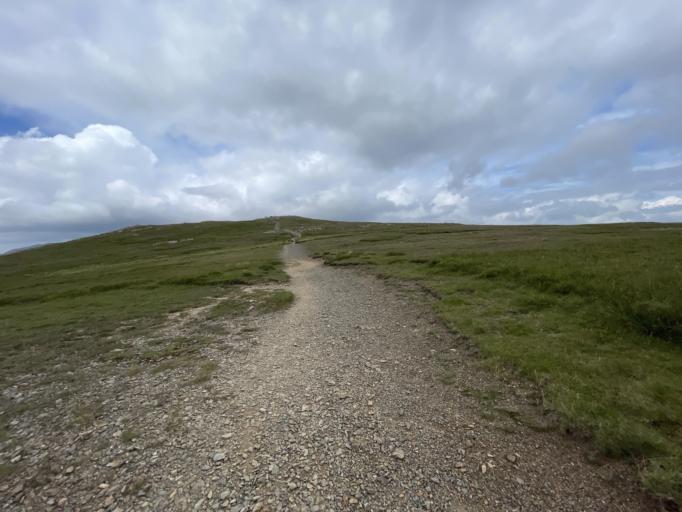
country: GB
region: England
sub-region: Cumbria
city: Keswick
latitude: 54.5393
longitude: -3.2351
